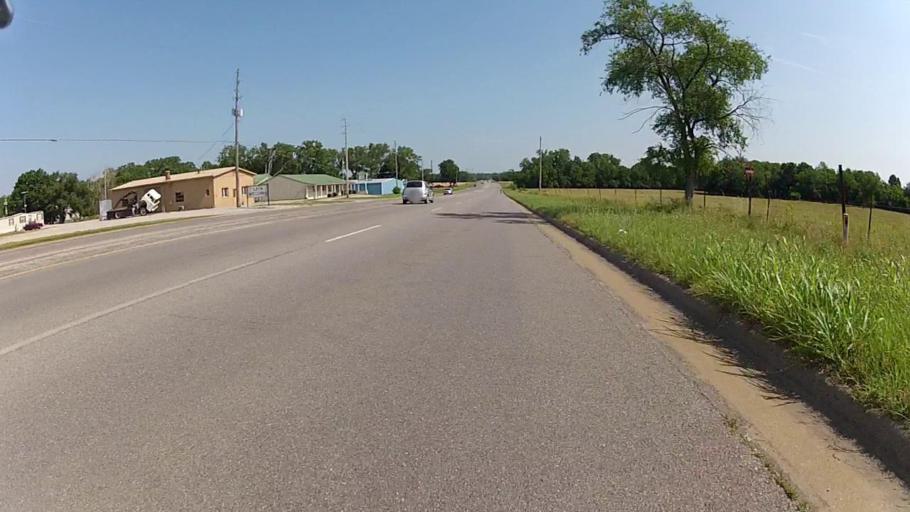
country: US
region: Kansas
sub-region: Montgomery County
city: Independence
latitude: 37.2056
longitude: -95.7106
